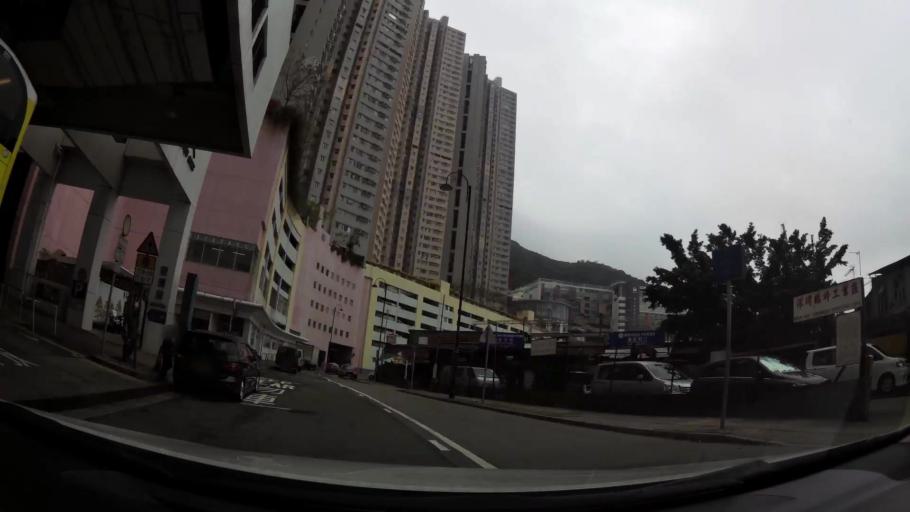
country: HK
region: Wanchai
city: Wan Chai
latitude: 22.2428
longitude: 114.1642
